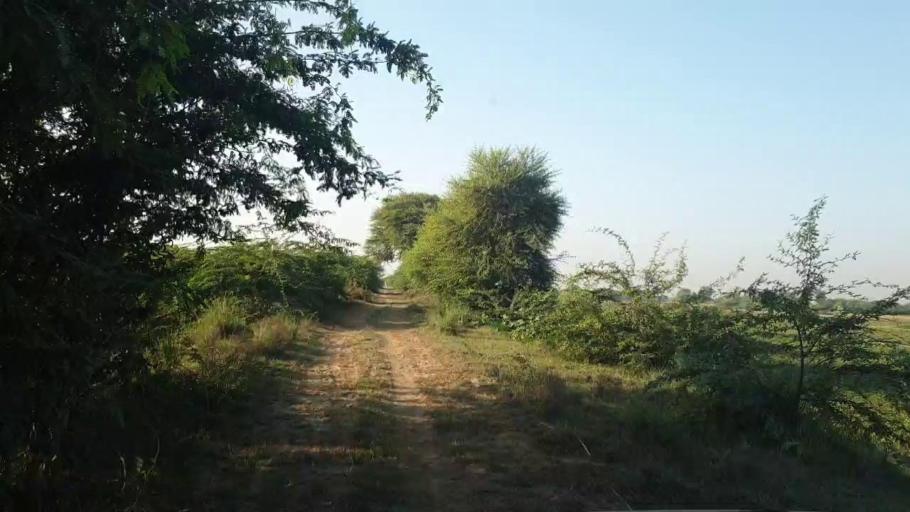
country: PK
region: Sindh
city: Badin
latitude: 24.6095
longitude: 68.7829
